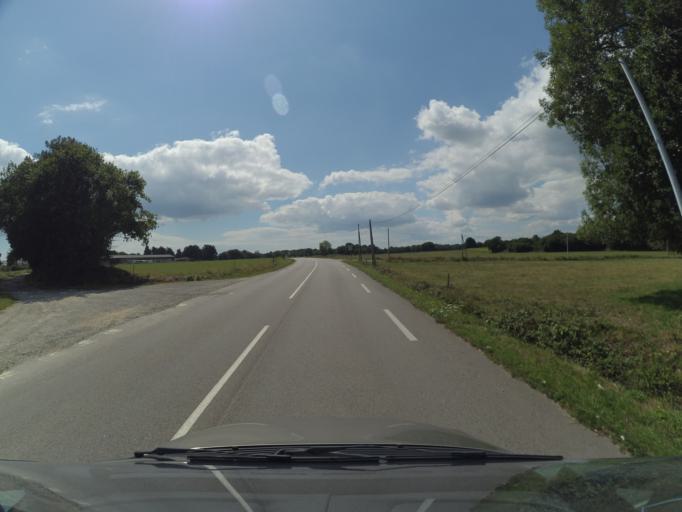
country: FR
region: Brittany
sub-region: Departement du Morbihan
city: Nostang
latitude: 47.7529
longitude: -3.1539
